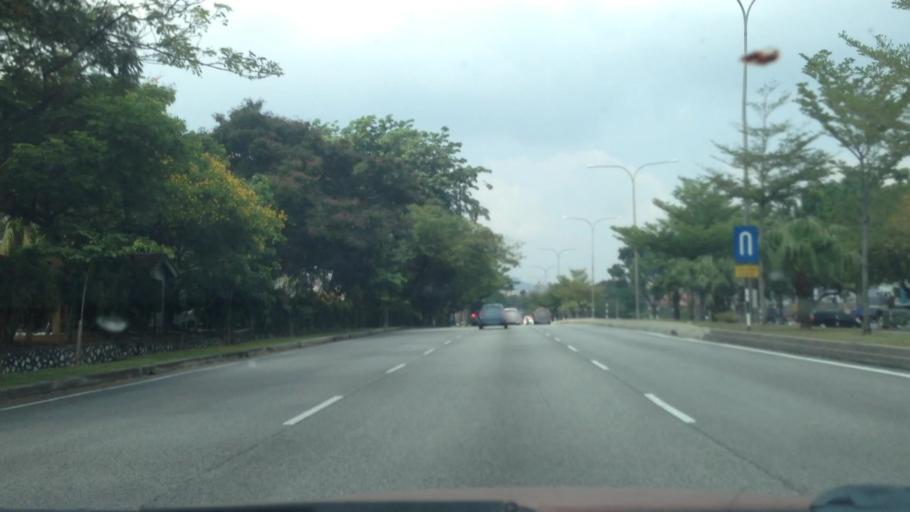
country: MY
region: Selangor
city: Subang Jaya
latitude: 3.0527
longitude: 101.5766
